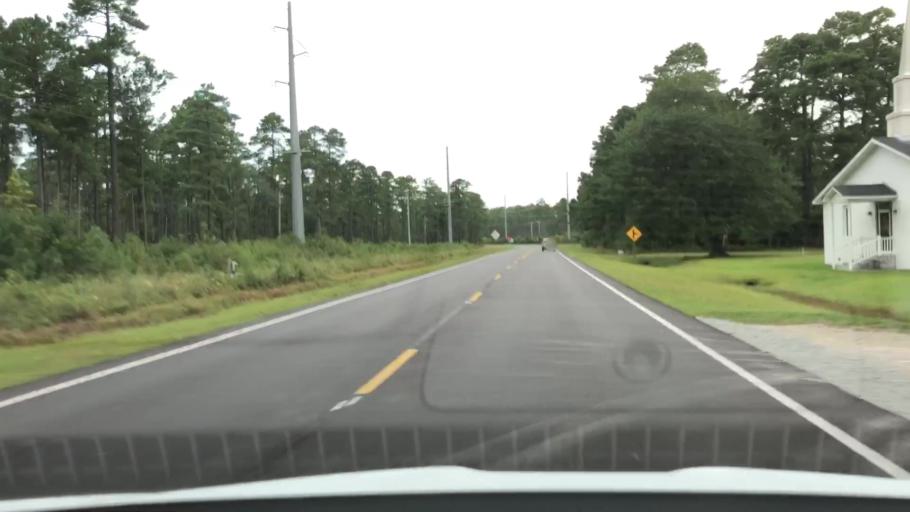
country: US
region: North Carolina
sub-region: Onslow County
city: Swansboro
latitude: 34.8056
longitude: -77.1334
